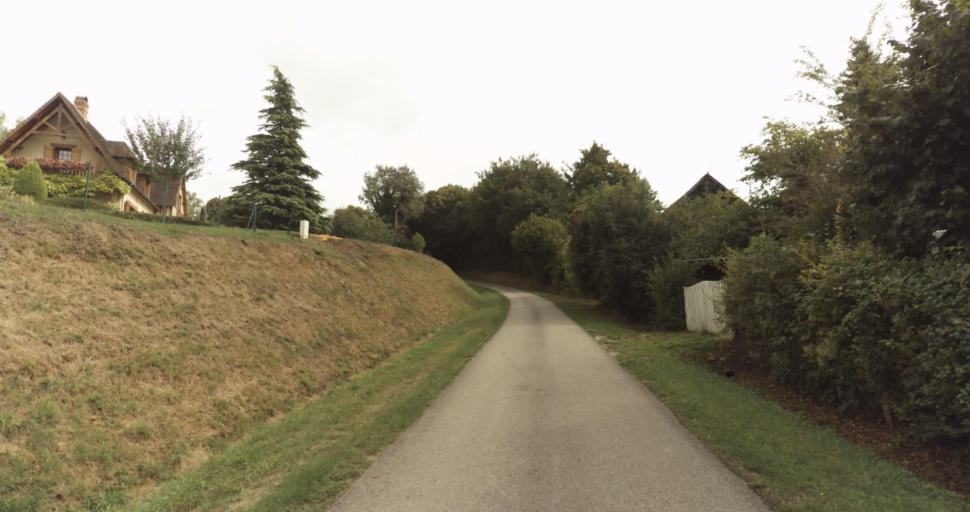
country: FR
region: Lower Normandy
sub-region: Departement de l'Orne
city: Gace
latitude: 48.8310
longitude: 0.2795
